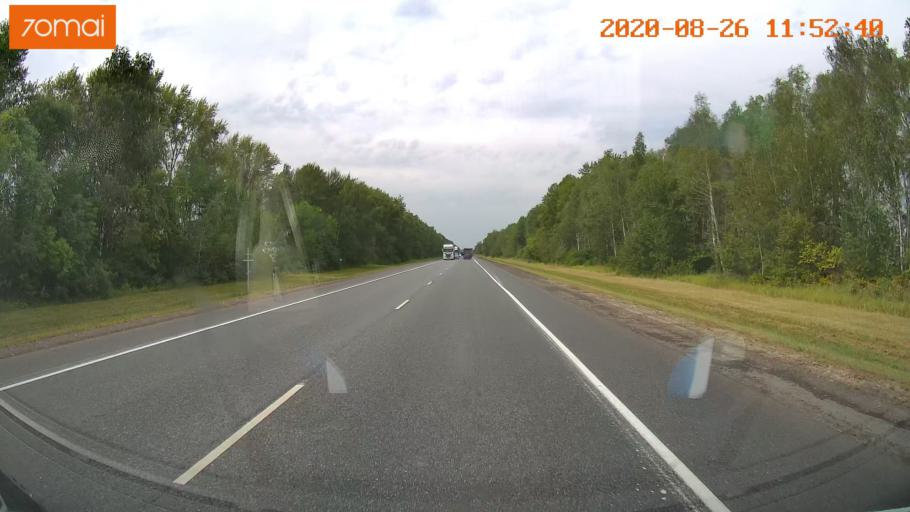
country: RU
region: Rjazan
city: Lesnoy
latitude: 54.2933
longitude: 40.4483
